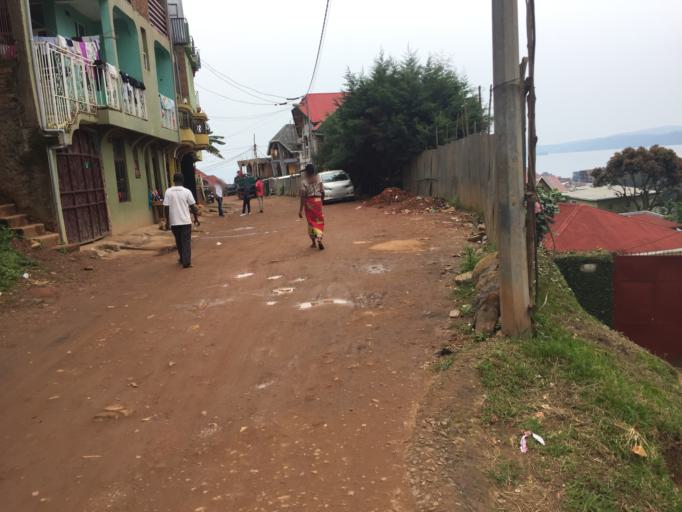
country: CD
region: South Kivu
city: Bukavu
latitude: -2.5021
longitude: 28.8620
